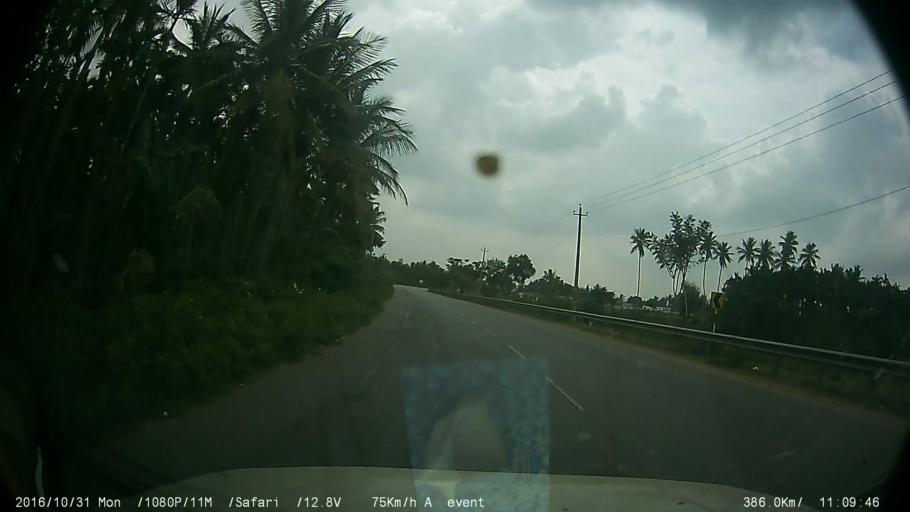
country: IN
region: Karnataka
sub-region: Mysore
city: Piriyapatna
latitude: 12.3504
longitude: 76.0697
